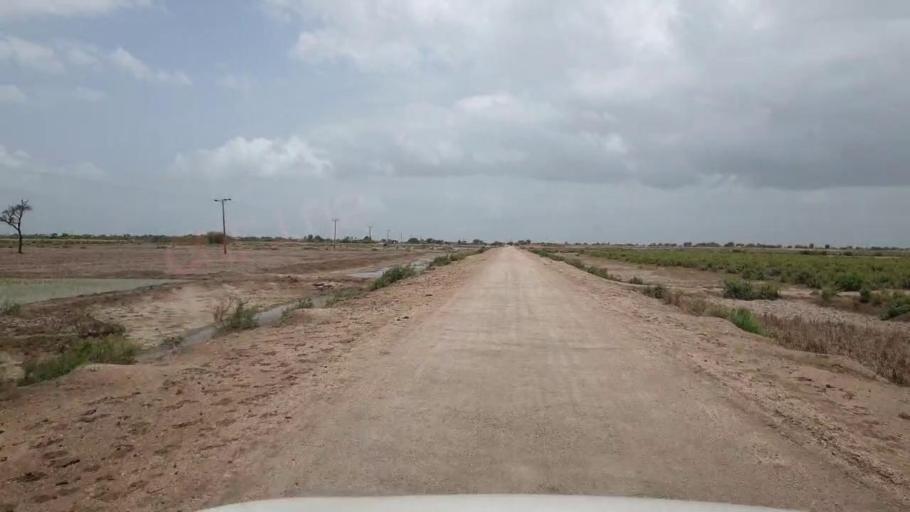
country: PK
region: Sindh
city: Kario
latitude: 24.6991
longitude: 68.6340
